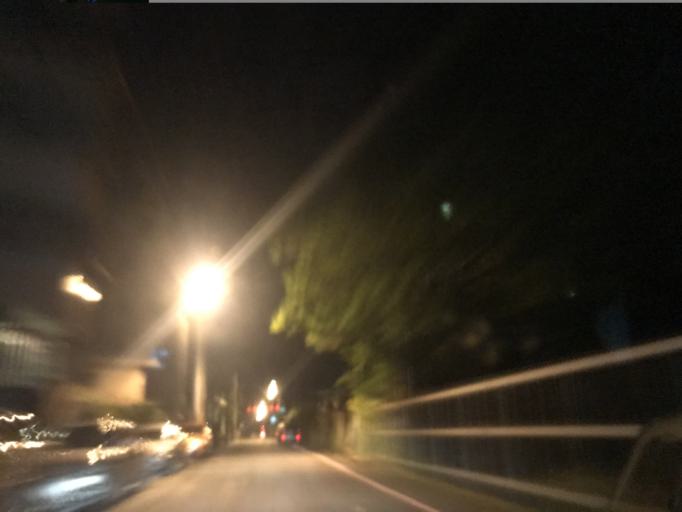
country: TW
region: Taiwan
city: Daxi
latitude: 24.8508
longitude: 121.2155
